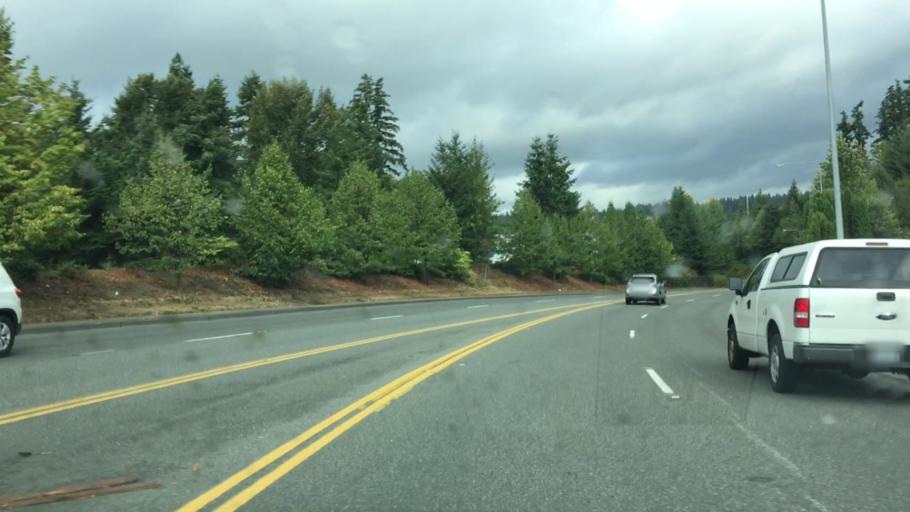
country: US
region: Washington
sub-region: King County
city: Woodinville
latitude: 47.7662
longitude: -122.1502
